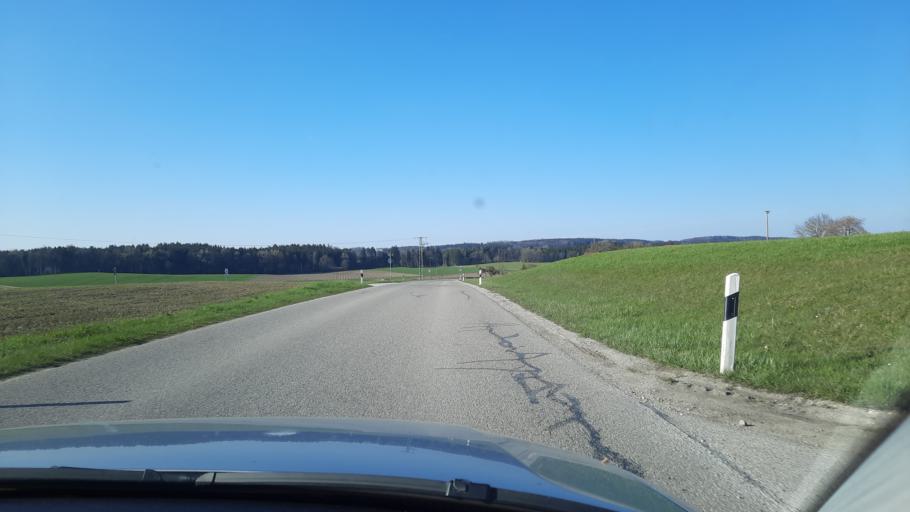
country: DE
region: Bavaria
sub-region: Upper Bavaria
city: Kirchseeon
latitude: 48.0495
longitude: 11.8965
